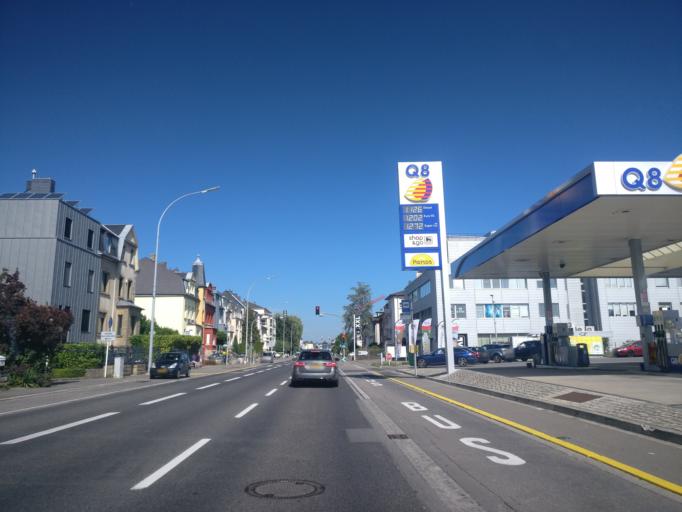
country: LU
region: Luxembourg
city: Bereldange
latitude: 49.6530
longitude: 6.1275
